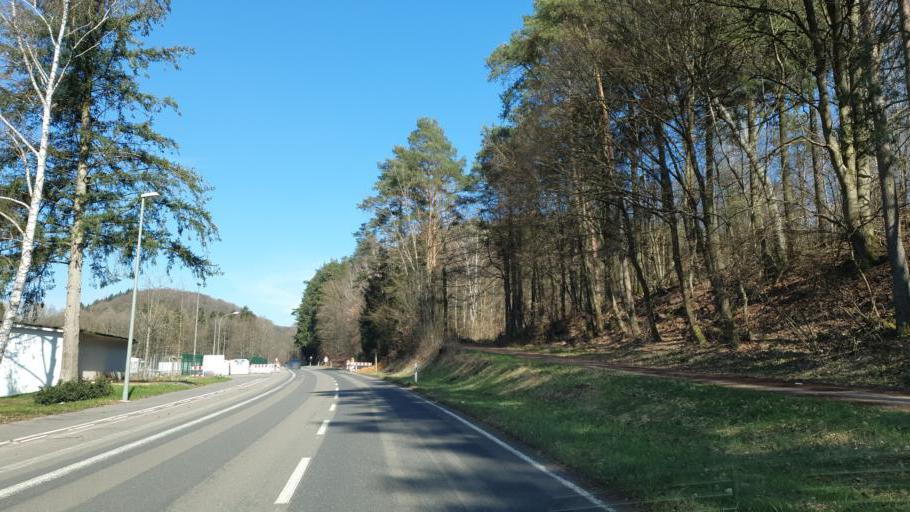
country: DE
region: Saarland
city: Beckingen
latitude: 49.3985
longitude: 6.7135
